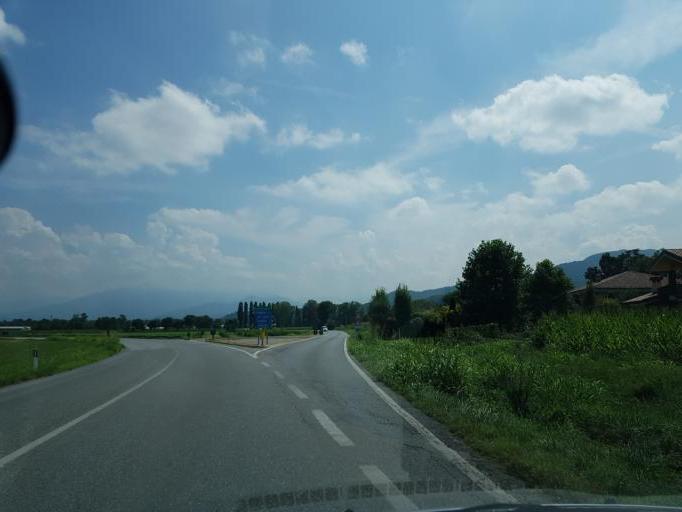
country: IT
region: Piedmont
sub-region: Provincia di Cuneo
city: Bernezzo
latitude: 44.4015
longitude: 7.4478
